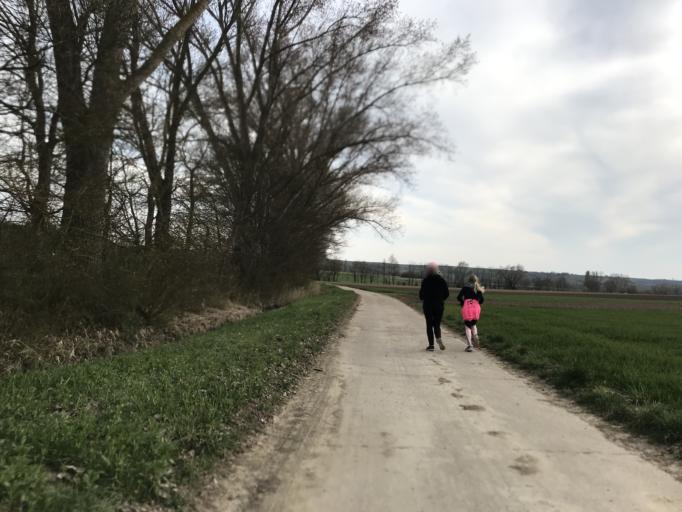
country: DE
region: Rheinland-Pfalz
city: Stadecken-Elsheim
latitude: 49.9005
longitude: 8.1235
